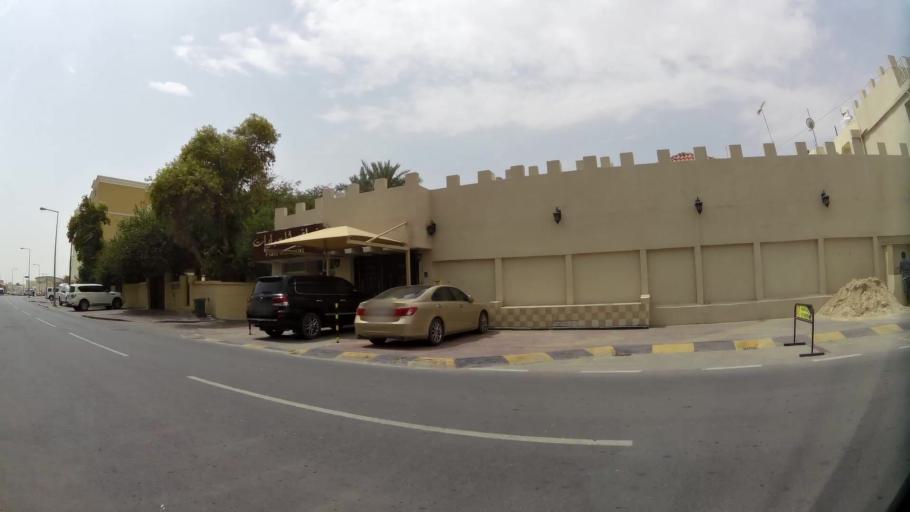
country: QA
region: Baladiyat ar Rayyan
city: Ar Rayyan
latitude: 25.3163
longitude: 51.4748
